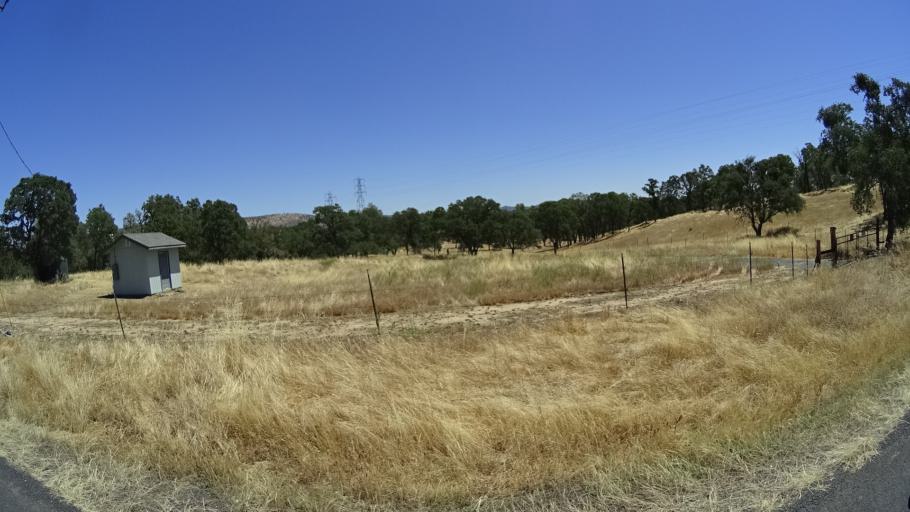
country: US
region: California
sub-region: Calaveras County
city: Copperopolis
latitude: 37.9648
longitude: -120.6738
